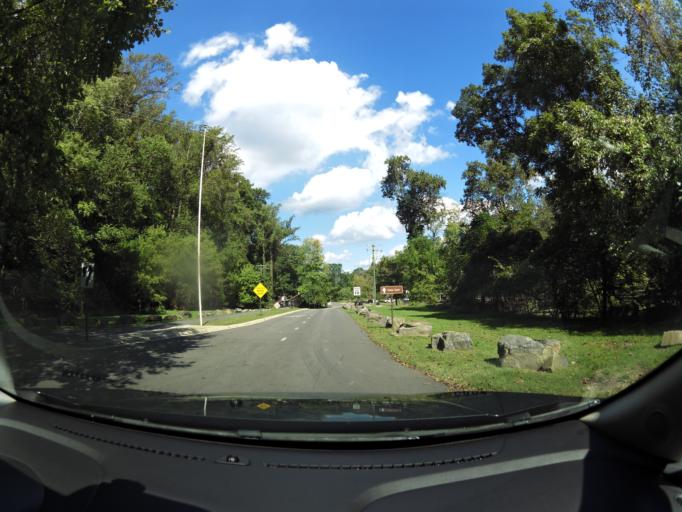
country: US
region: Virginia
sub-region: Fairfax County
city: Great Falls
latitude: 38.9953
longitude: -77.2553
